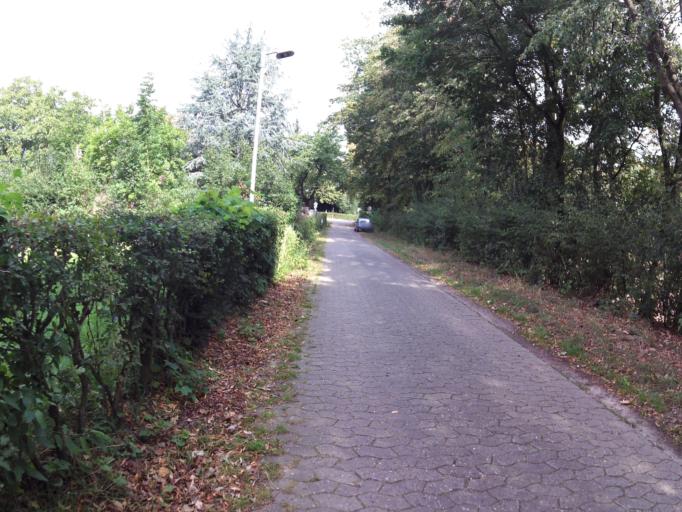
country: DE
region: Lower Saxony
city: Landesbergen
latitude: 52.5753
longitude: 9.1138
